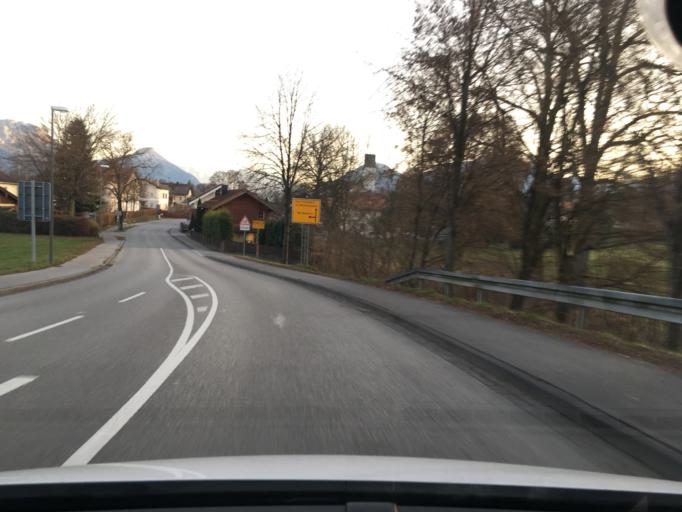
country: DE
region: Bavaria
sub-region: Upper Bavaria
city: Raubling
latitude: 47.7824
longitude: 12.1075
